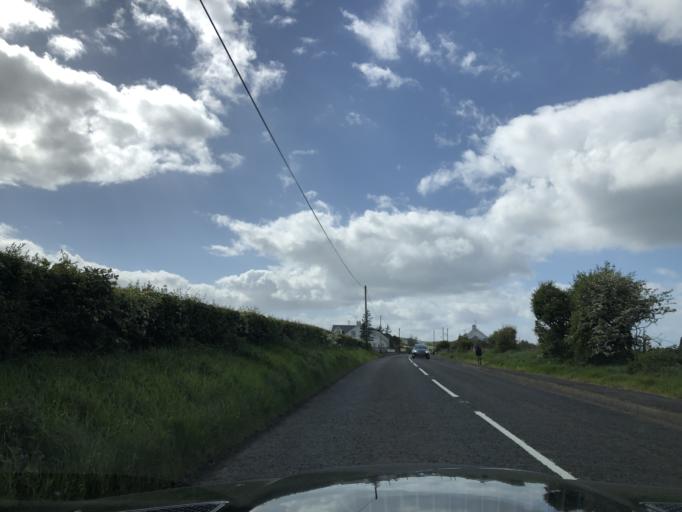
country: GB
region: Northern Ireland
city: Bushmills
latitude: 55.2073
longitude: -6.5378
